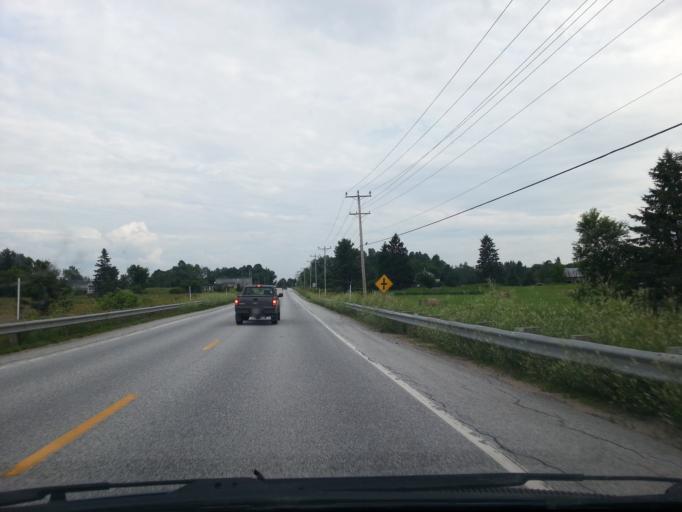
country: CA
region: Quebec
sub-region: Outaouais
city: Wakefield
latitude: 45.8742
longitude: -76.0248
